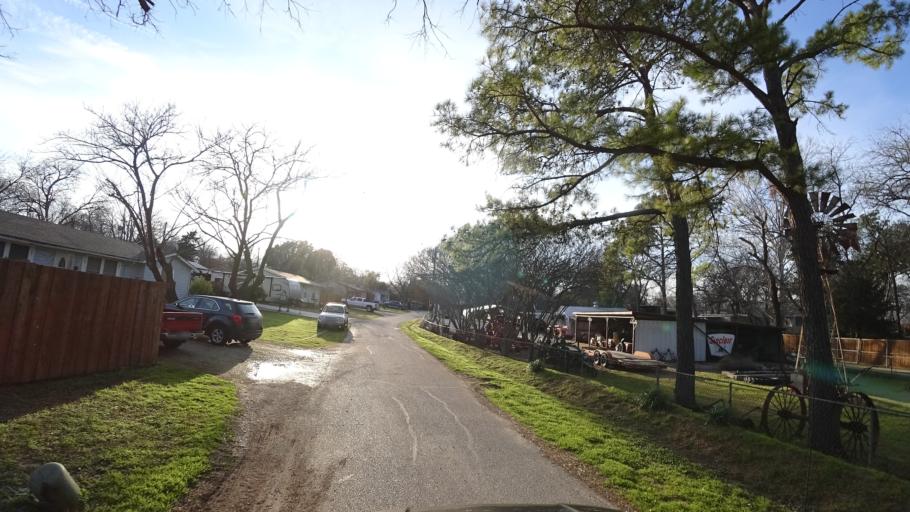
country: US
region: Texas
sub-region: Denton County
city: Lewisville
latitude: 33.0509
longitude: -96.9968
